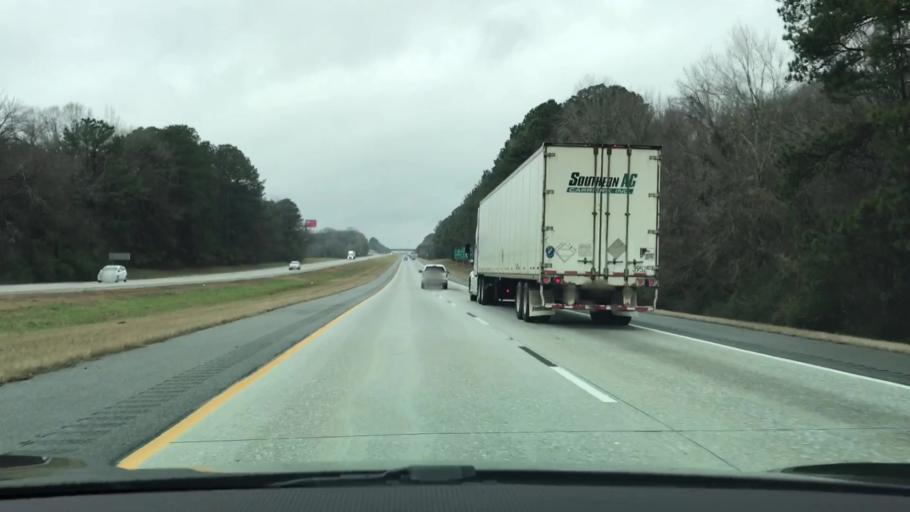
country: US
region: Georgia
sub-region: Putnam County
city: Jefferson
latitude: 33.5469
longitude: -83.3407
